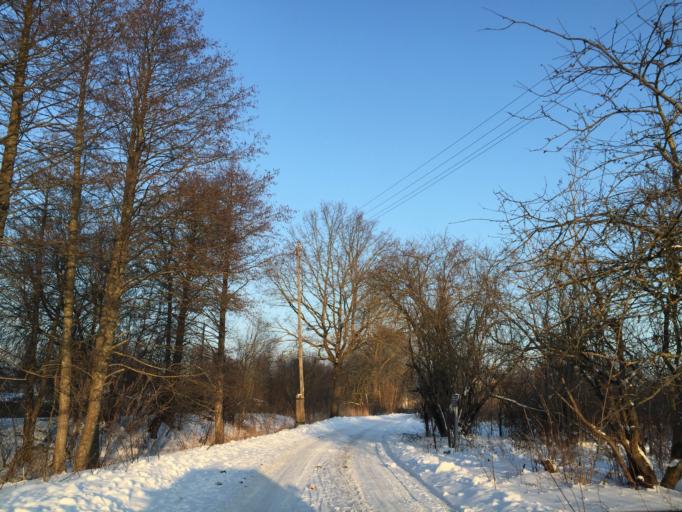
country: LV
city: Tireli
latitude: 56.9370
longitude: 23.6084
